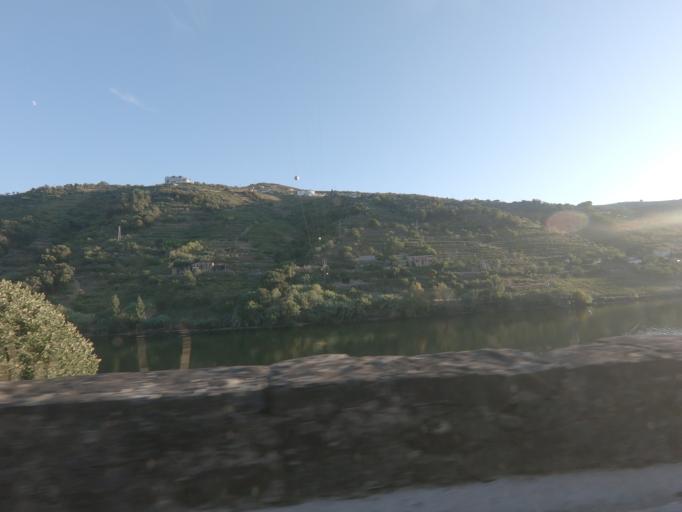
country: PT
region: Vila Real
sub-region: Mesao Frio
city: Mesao Frio
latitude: 41.1558
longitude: -7.8410
